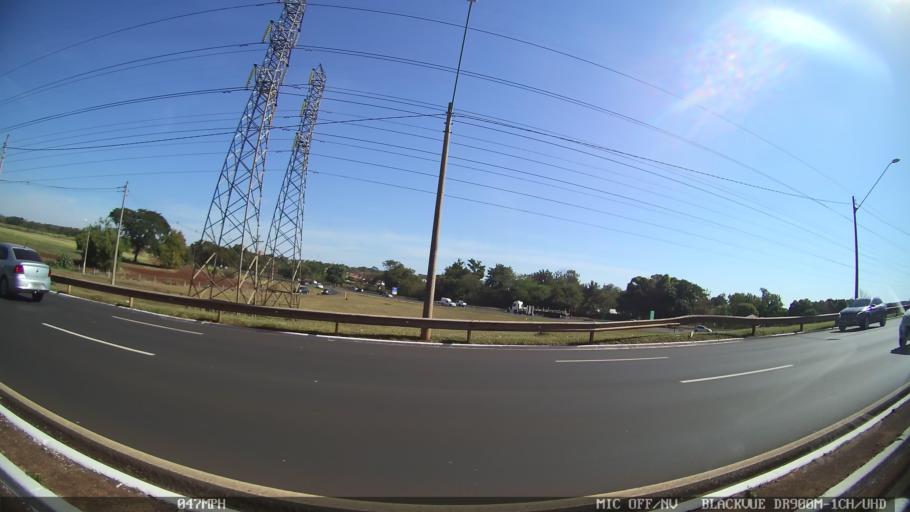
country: BR
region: Sao Paulo
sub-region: Ribeirao Preto
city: Ribeirao Preto
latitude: -21.2161
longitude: -47.7725
